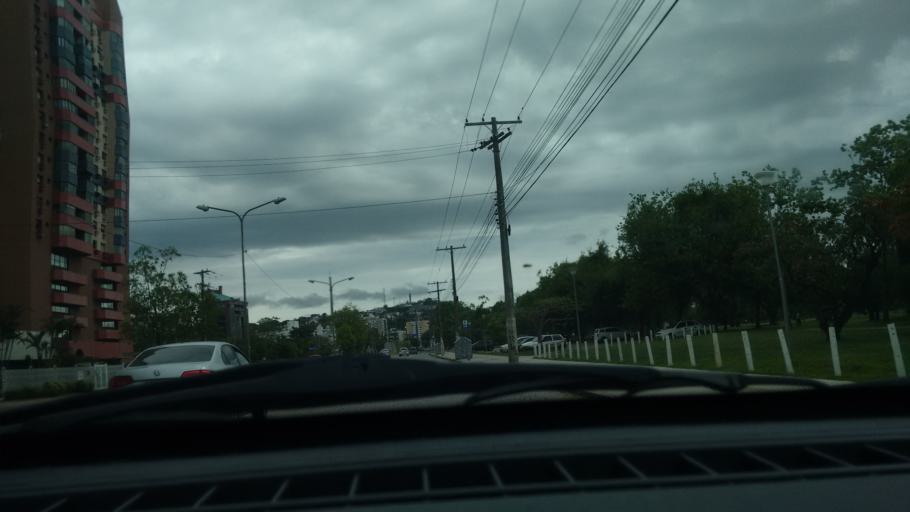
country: BR
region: Rio Grande do Sul
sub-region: Porto Alegre
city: Porto Alegre
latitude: -30.0551
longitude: -51.2304
